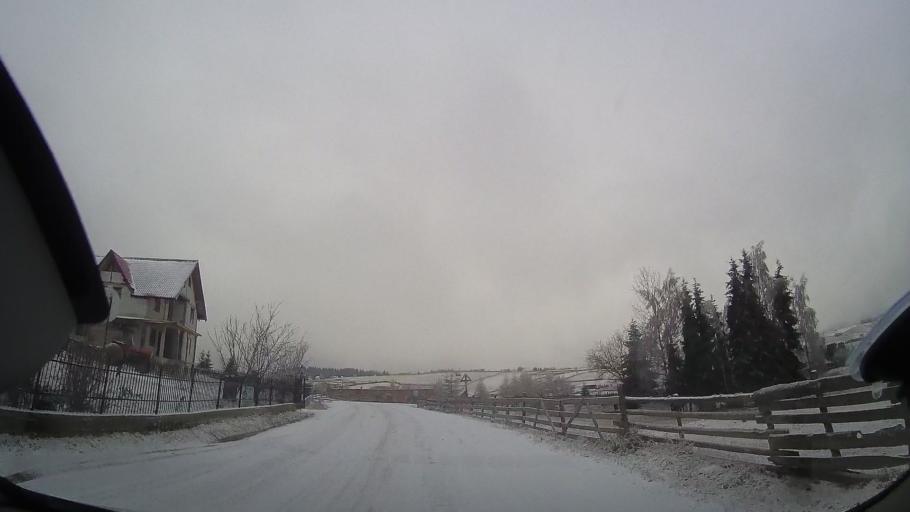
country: RO
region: Cluj
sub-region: Comuna Marisel
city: Marisel
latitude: 46.6619
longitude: 23.1185
